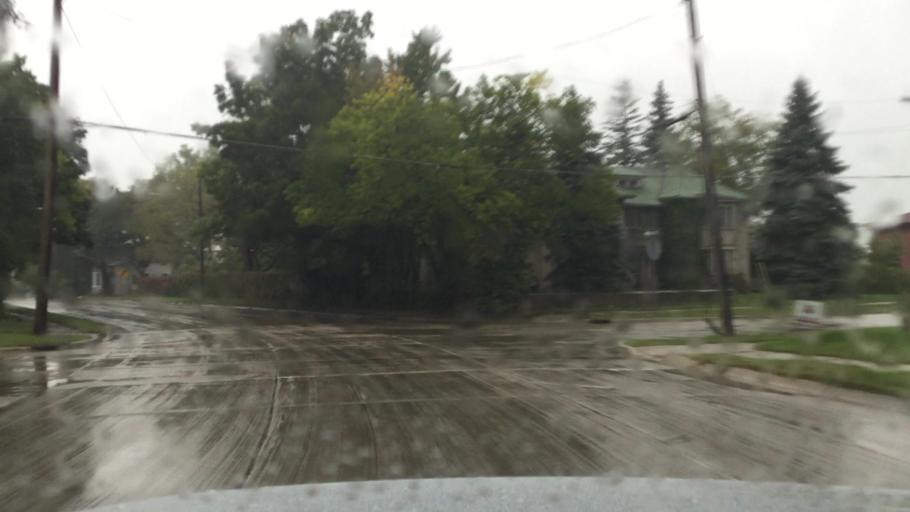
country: US
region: Michigan
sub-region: Saginaw County
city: Saginaw
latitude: 43.4178
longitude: -83.9414
